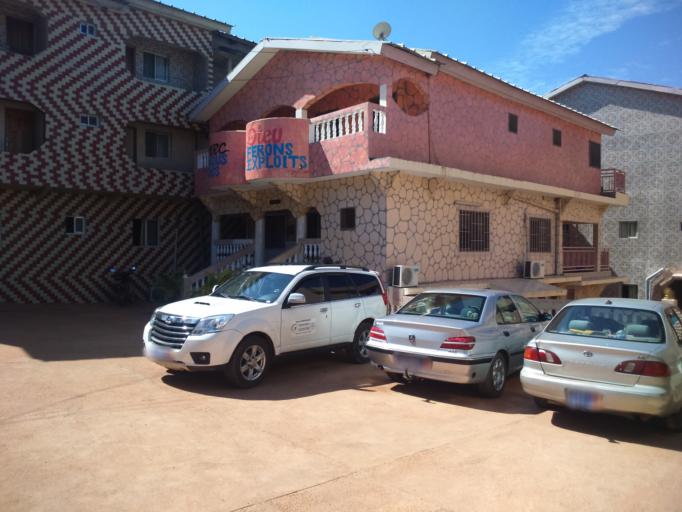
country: CI
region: Agneby
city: Agboville
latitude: 5.9157
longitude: -4.2122
